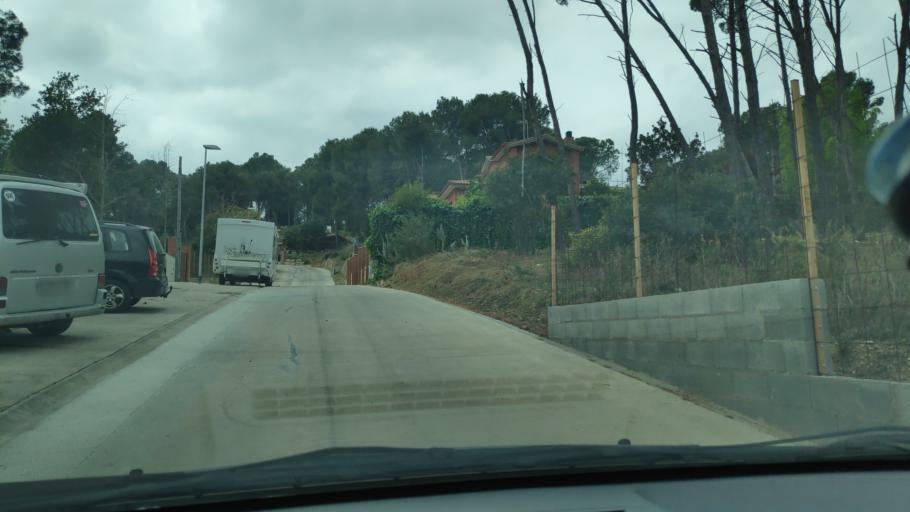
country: ES
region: Catalonia
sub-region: Provincia de Barcelona
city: Sant Quirze del Valles
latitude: 41.5172
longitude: 2.0900
